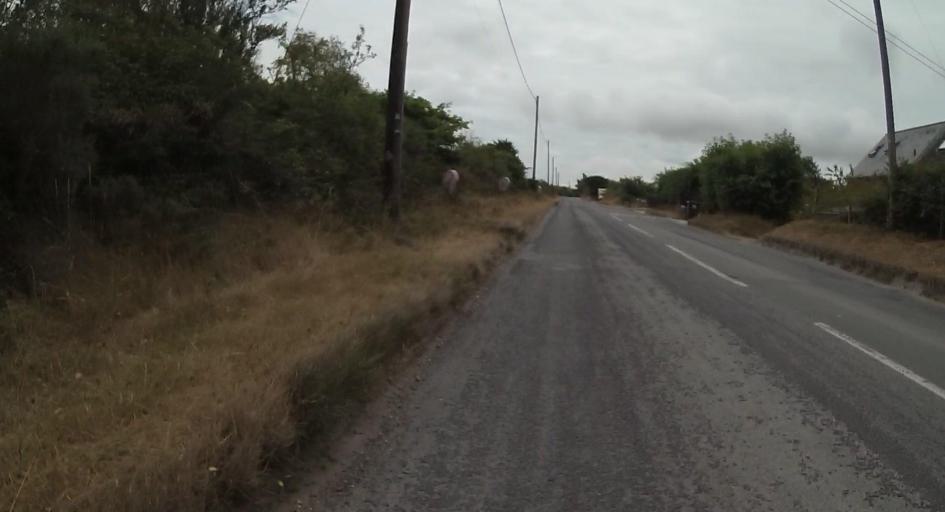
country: GB
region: England
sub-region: Dorset
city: Wareham
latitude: 50.6626
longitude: -2.1010
